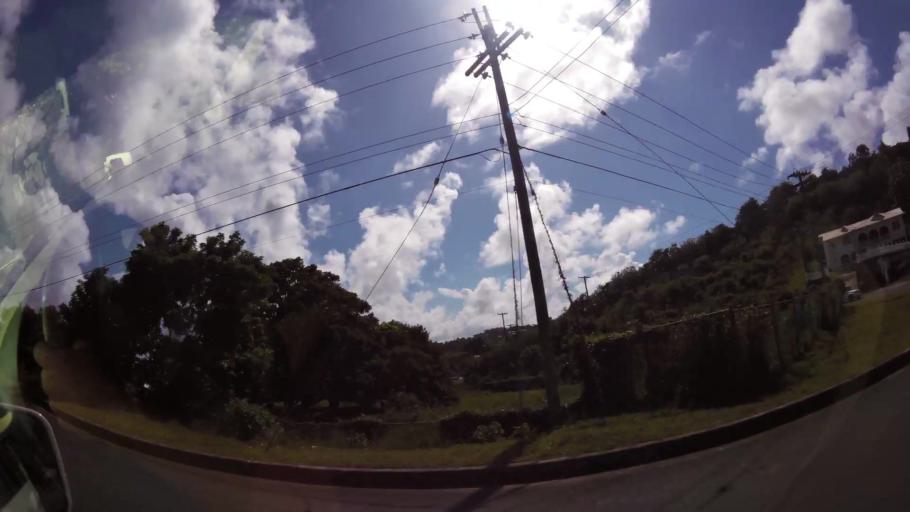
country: VC
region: Saint George
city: Kingstown
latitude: 13.1449
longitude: -61.1697
